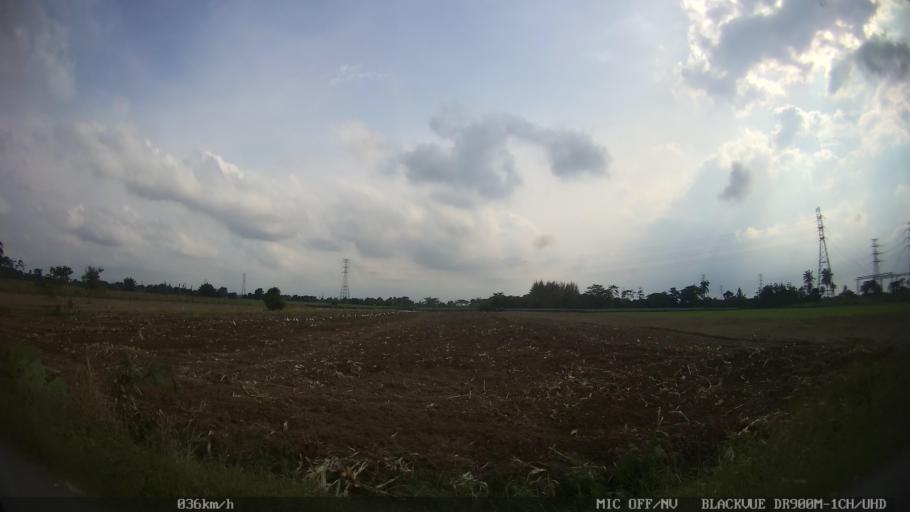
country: ID
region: North Sumatra
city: Percut
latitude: 3.5666
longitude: 98.7845
